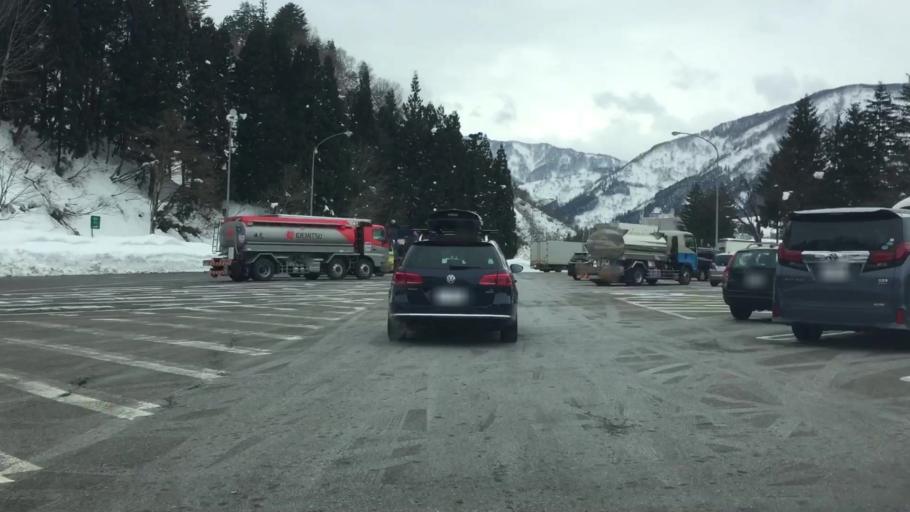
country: JP
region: Niigata
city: Shiozawa
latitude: 36.9802
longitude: 138.8126
